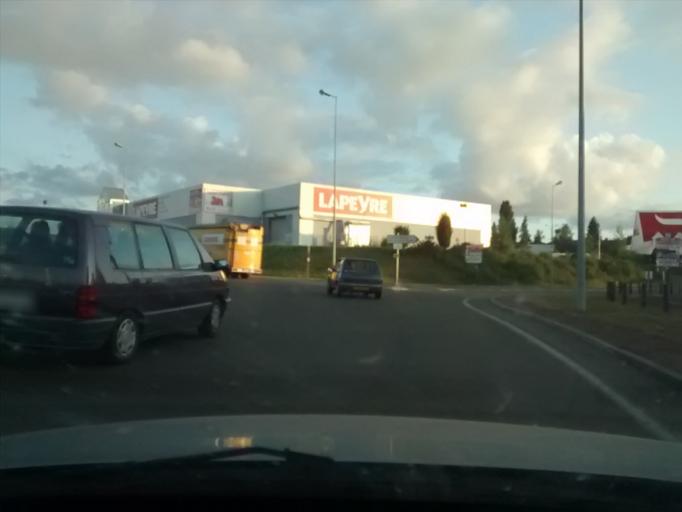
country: FR
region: Pays de la Loire
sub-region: Departement de la Sarthe
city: La Chapelle-Saint-Aubin
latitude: 48.0494
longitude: 0.1699
